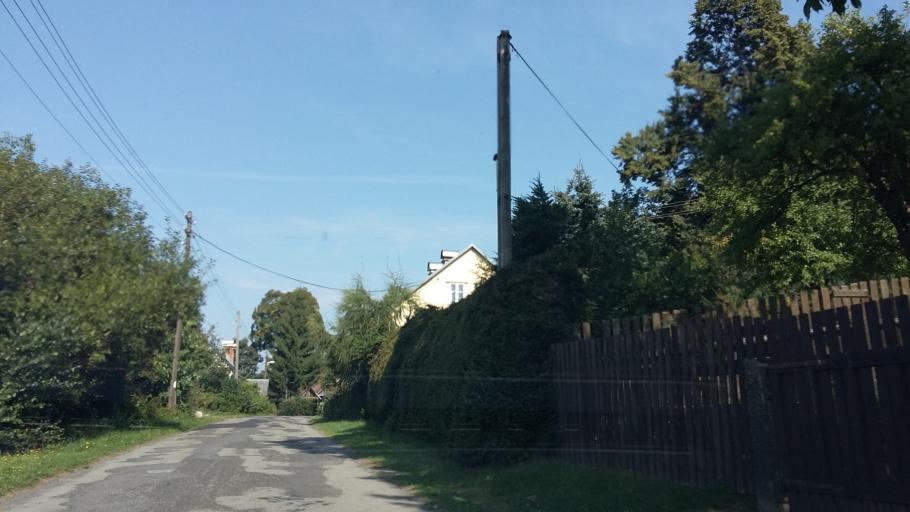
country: CZ
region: Liberecky
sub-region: Okres Jablonec nad Nisou
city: Lucany nad Nisou
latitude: 50.7524
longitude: 15.1931
